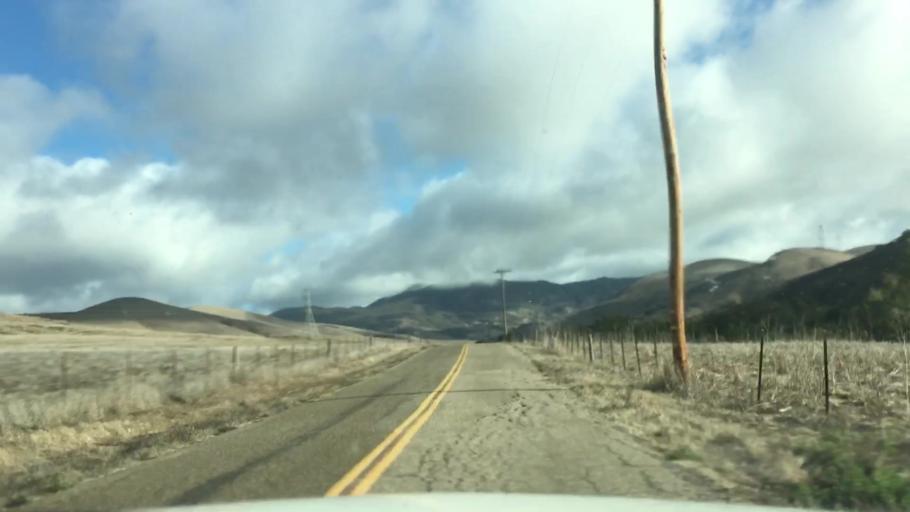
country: US
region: California
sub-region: San Luis Obispo County
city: Morro Bay
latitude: 35.3743
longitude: -120.7971
